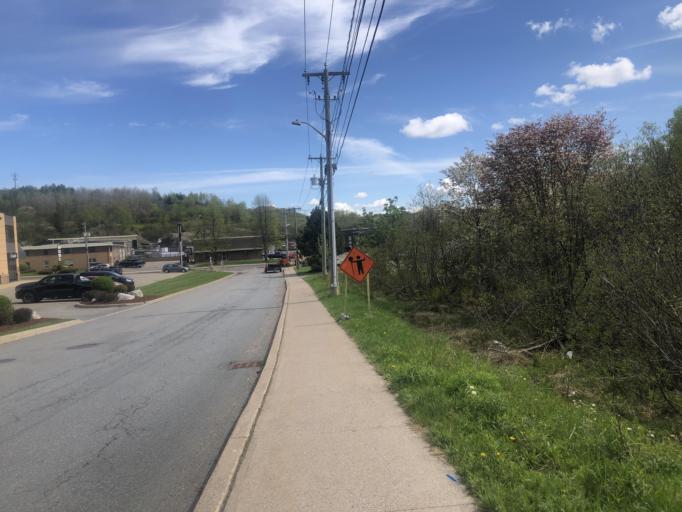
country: CA
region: New Brunswick
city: Saint John
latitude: 45.2868
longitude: -66.0814
